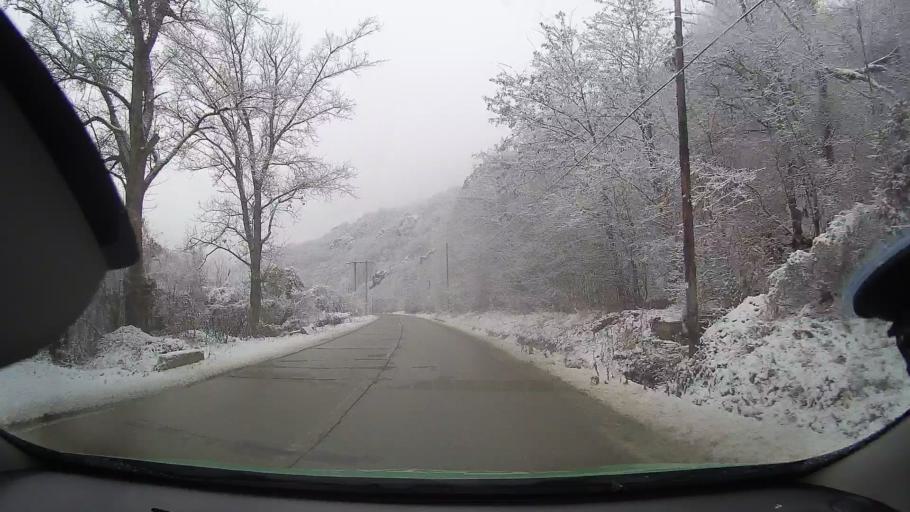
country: RO
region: Cluj
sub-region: Comuna Moldovenesti
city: Moldovenesti
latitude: 46.5085
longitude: 23.6449
